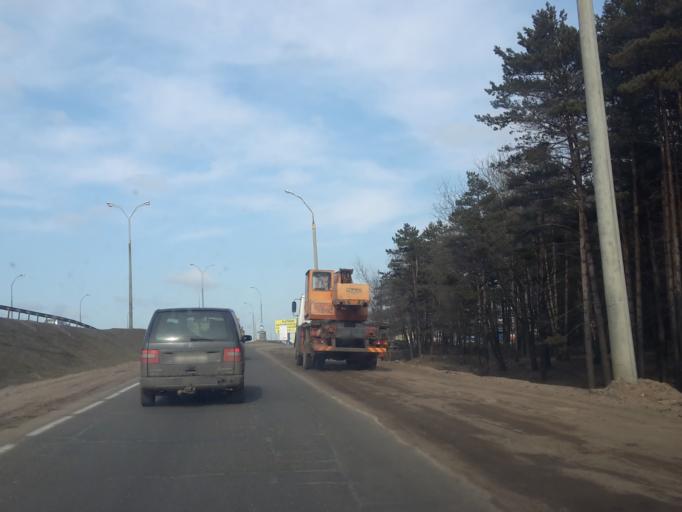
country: BY
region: Minsk
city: Vyaliki Trastsyanets
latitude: 53.9104
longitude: 27.6862
